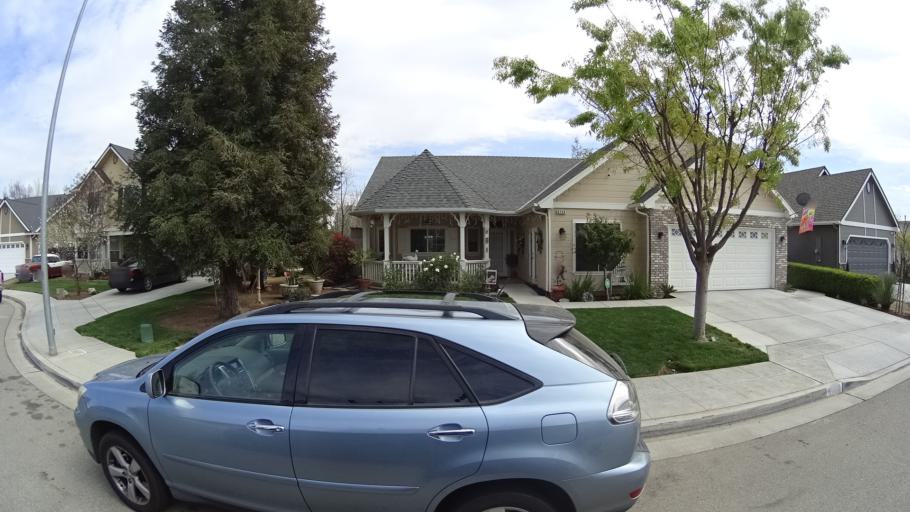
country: US
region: California
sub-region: Fresno County
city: Biola
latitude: 36.8360
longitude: -119.8903
